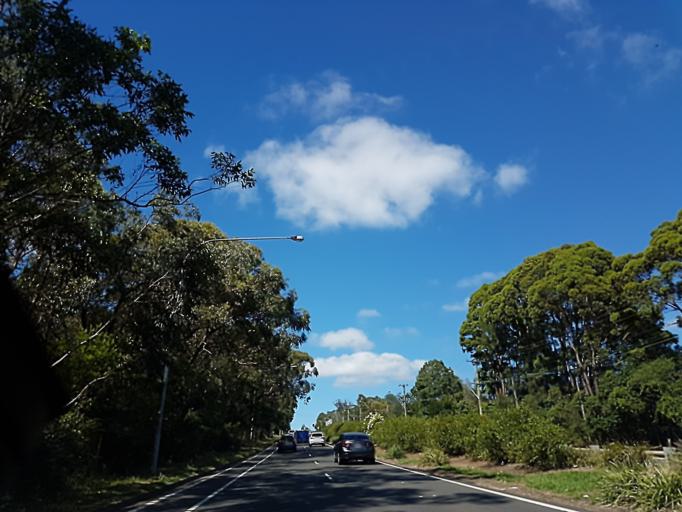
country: AU
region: New South Wales
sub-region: Warringah
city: Davidson
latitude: -33.7138
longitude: 151.2173
